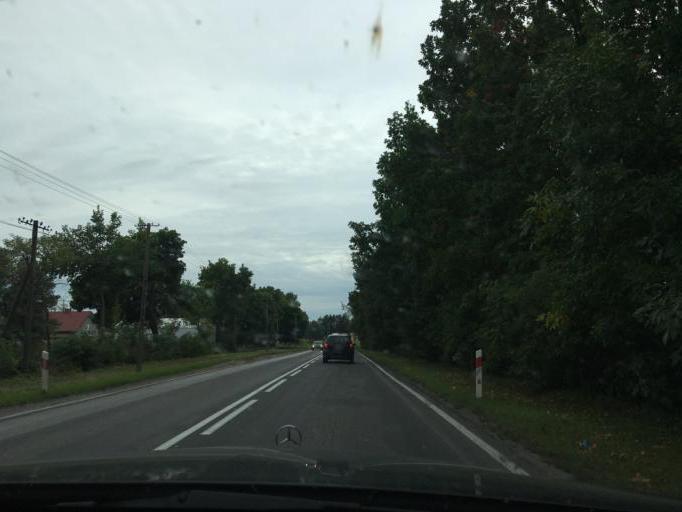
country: PL
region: Masovian Voivodeship
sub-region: Powiat ostrowski
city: Ostrow Mazowiecka
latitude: 52.8343
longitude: 21.8732
